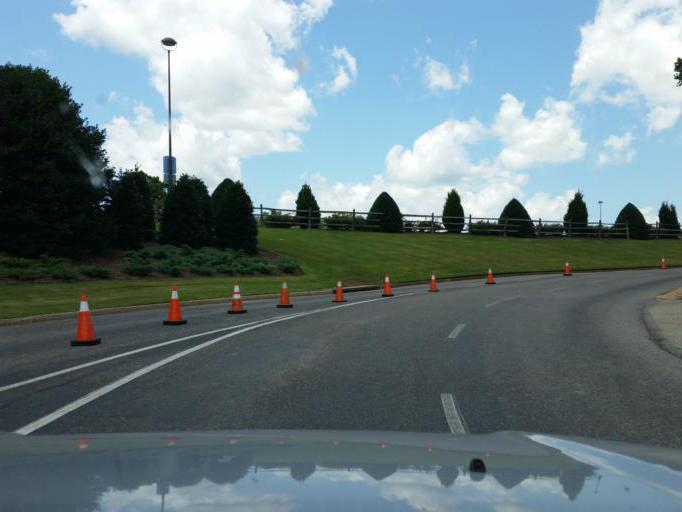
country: US
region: Virginia
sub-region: City of Williamsburg
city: Williamsburg
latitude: 37.2363
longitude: -76.6424
